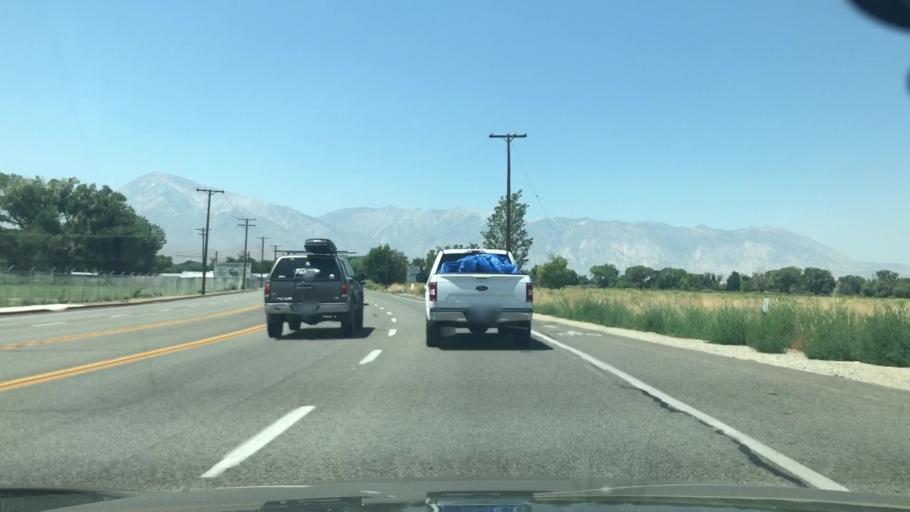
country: US
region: California
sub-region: Inyo County
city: Bishop
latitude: 37.3743
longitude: -118.3979
